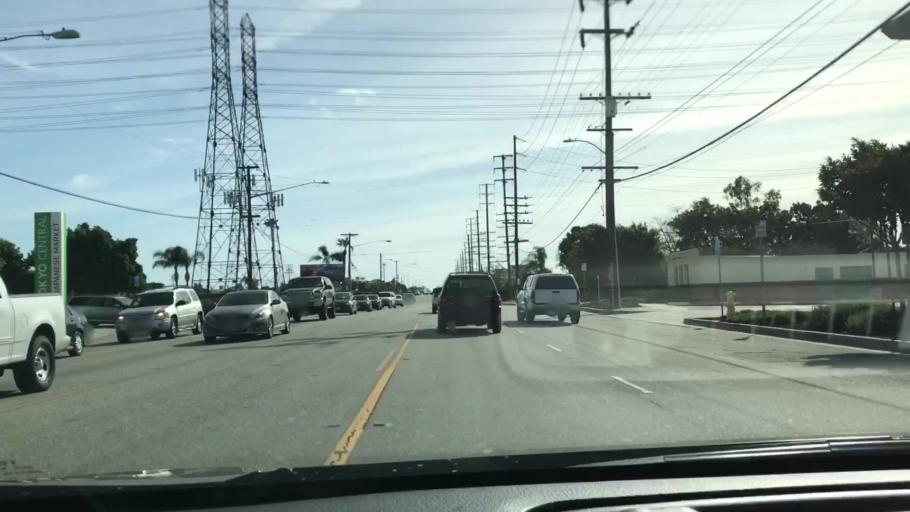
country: US
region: California
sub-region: Los Angeles County
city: Gardena
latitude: 33.8719
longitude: -118.3092
